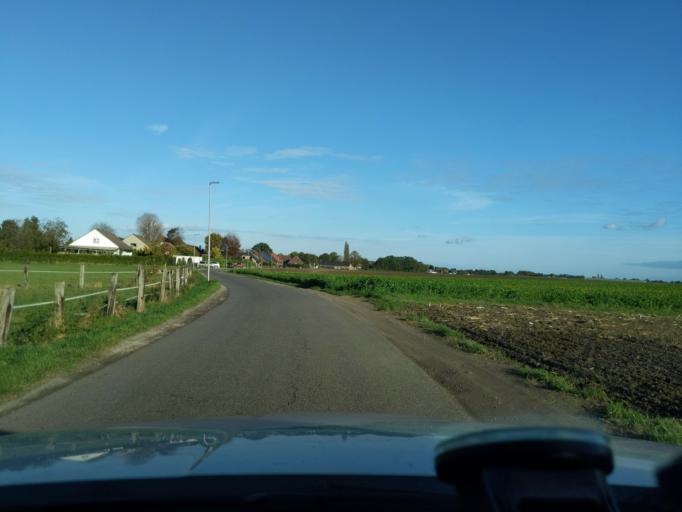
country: DE
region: North Rhine-Westphalia
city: Kempen
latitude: 51.3966
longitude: 6.4291
